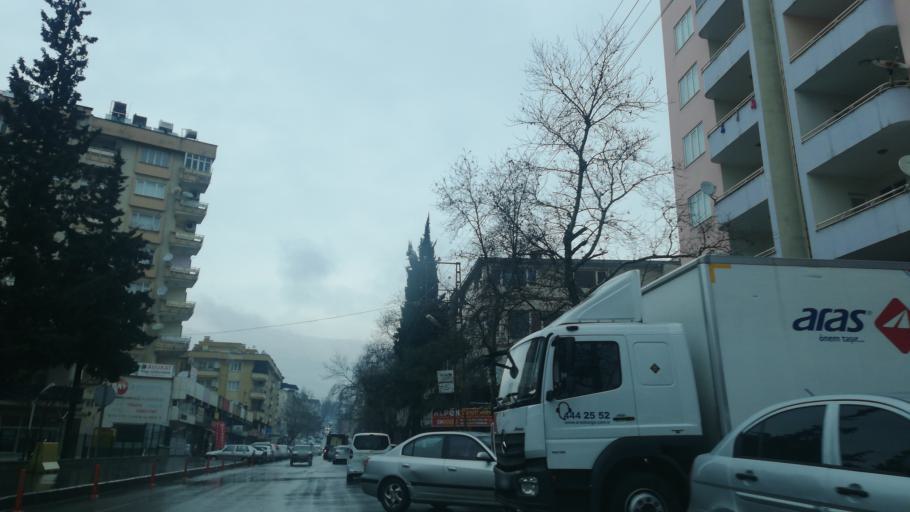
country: TR
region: Kahramanmaras
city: Kahramanmaras
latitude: 37.5787
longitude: 36.9327
